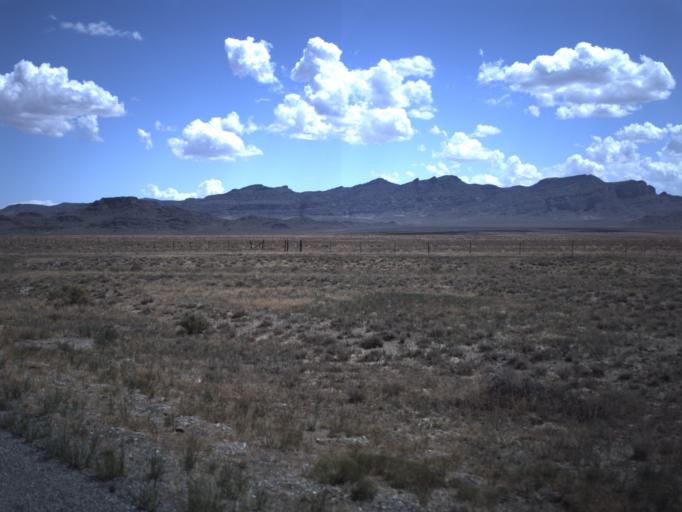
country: US
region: Utah
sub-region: Beaver County
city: Milford
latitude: 39.0538
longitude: -113.7748
